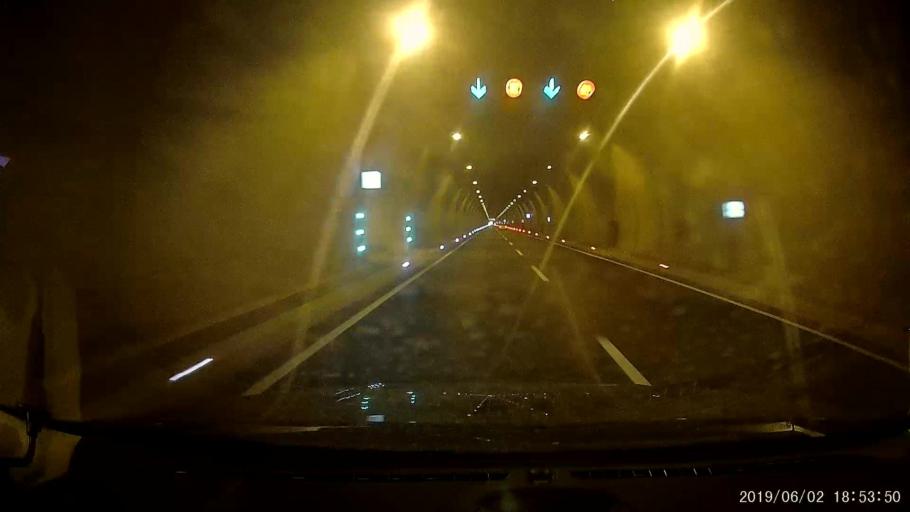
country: TR
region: Ordu
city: Ordu
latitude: 40.9739
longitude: 37.8387
